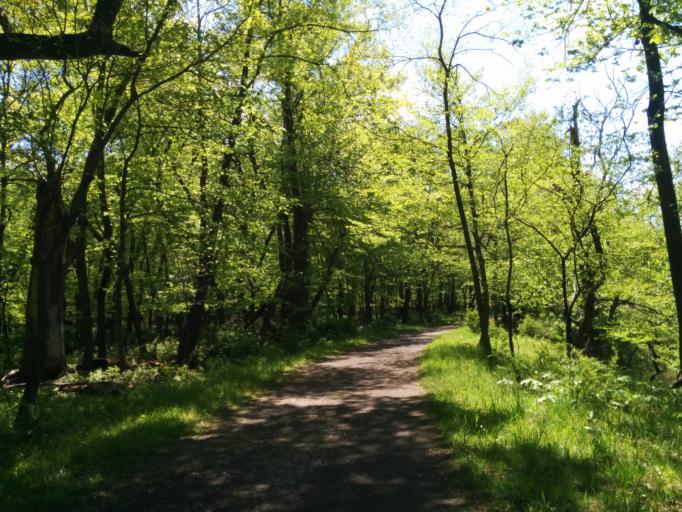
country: US
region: Illinois
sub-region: Cook County
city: Schiller Park
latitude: 41.9716
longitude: -87.8540
